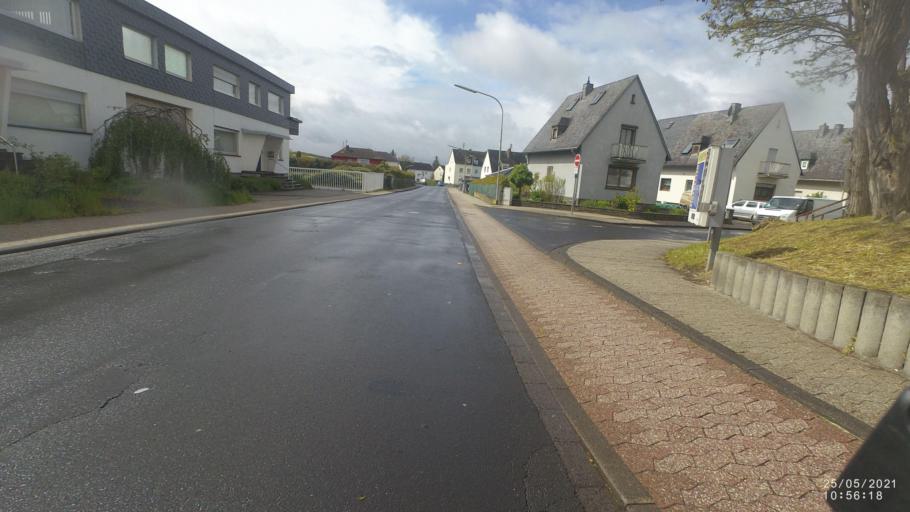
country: DE
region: Rheinland-Pfalz
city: Mayen
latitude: 50.3254
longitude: 7.2440
